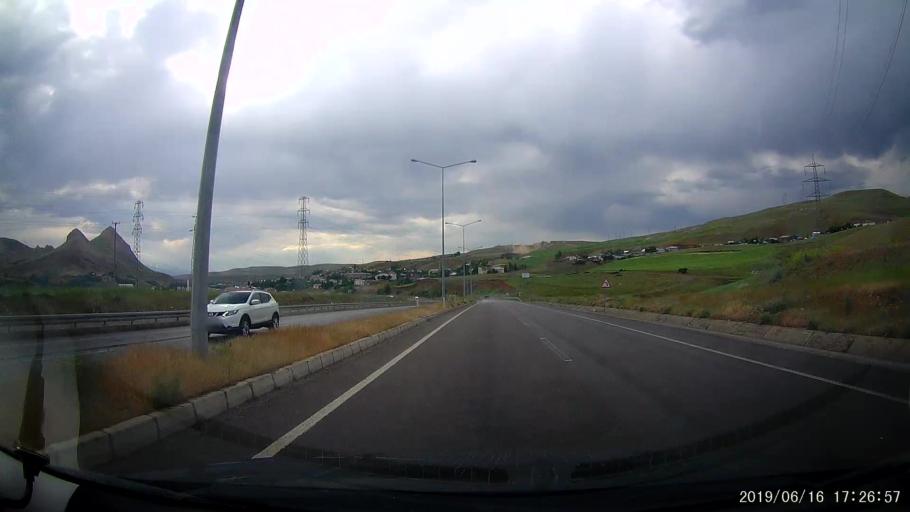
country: TR
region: Erzincan
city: Tercan
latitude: 39.7732
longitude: 40.4023
